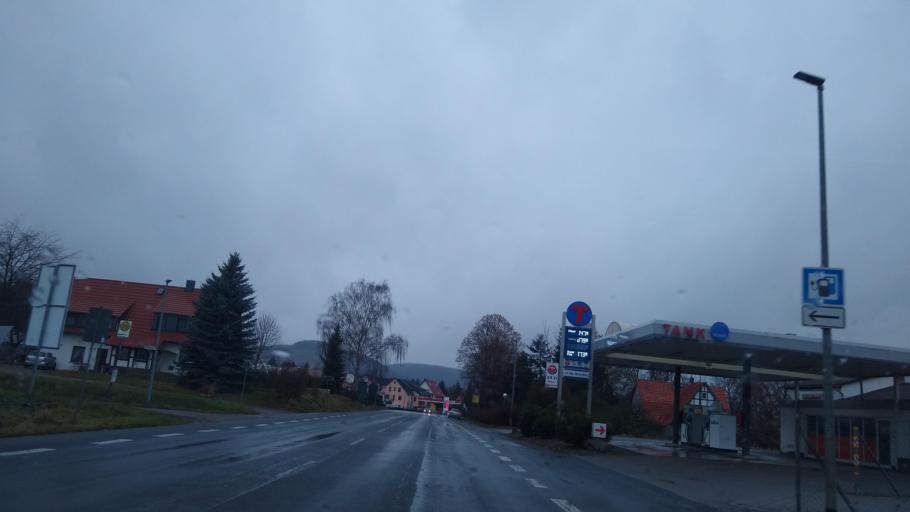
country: DE
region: Lower Saxony
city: Hehlen
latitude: 51.9847
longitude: 9.4817
